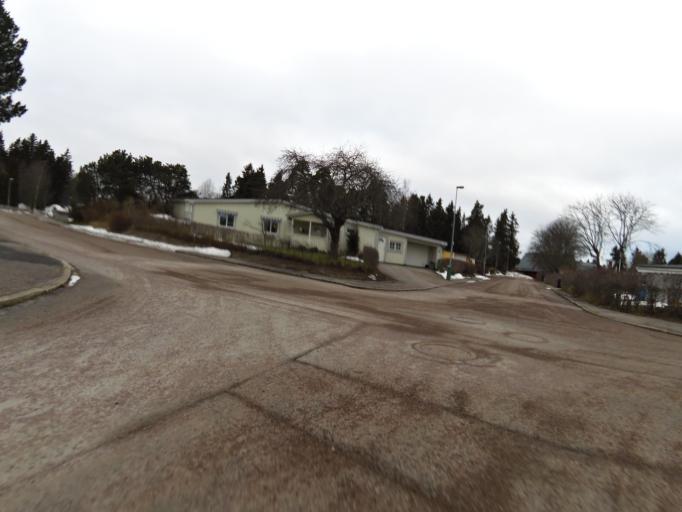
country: SE
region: Gaevleborg
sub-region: Gavle Kommun
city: Gavle
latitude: 60.6577
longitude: 17.1463
